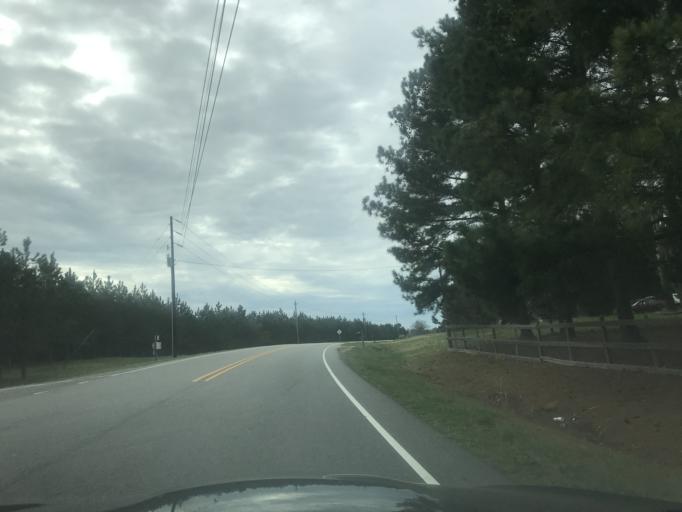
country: US
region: North Carolina
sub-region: Franklin County
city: Louisburg
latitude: 36.0868
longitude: -78.3796
